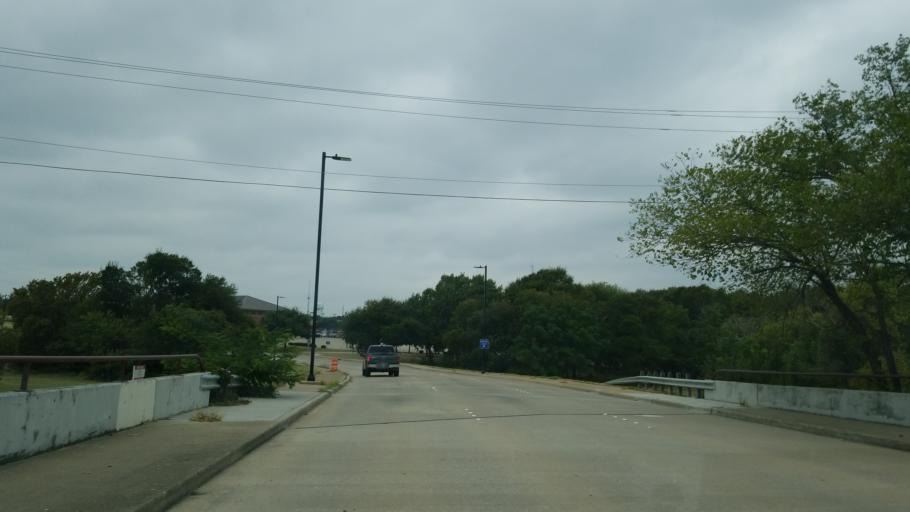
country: US
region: Texas
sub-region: Dallas County
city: Garland
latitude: 32.9110
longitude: -96.6520
